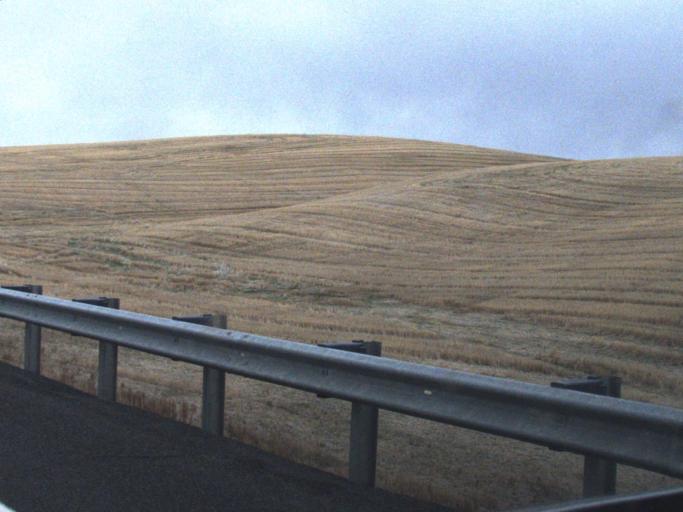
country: US
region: Washington
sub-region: Whitman County
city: Colfax
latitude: 46.8107
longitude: -117.7076
